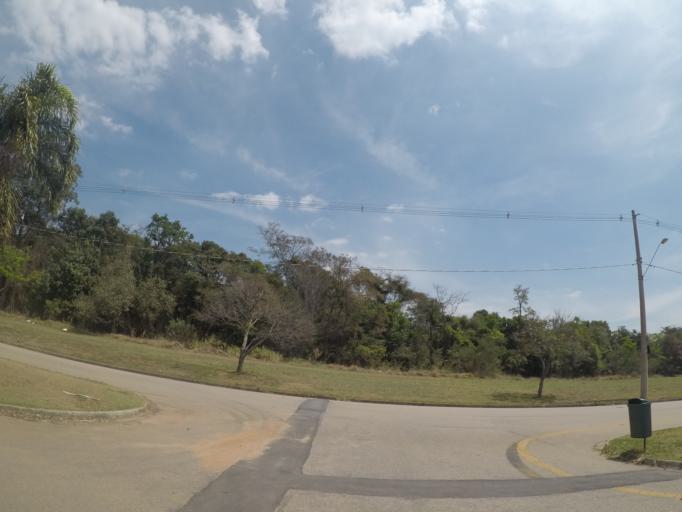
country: BR
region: Sao Paulo
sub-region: Itupeva
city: Itupeva
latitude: -23.2496
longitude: -47.0473
